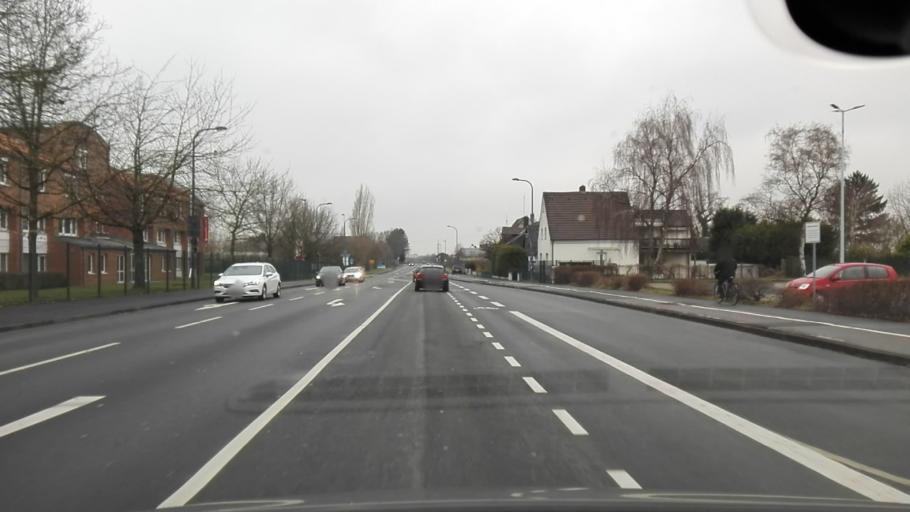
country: DE
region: North Rhine-Westphalia
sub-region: Regierungsbezirk Arnsberg
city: Unna
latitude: 51.5638
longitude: 7.6790
